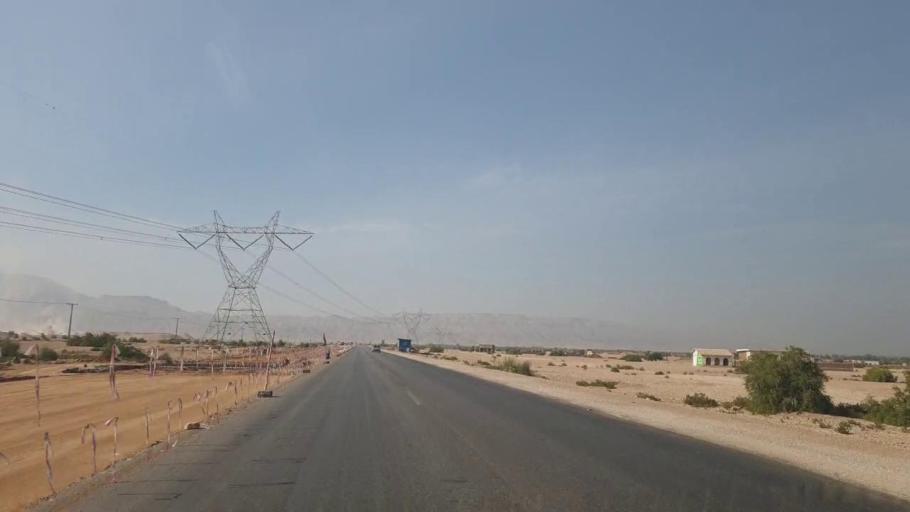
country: PK
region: Sindh
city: Sehwan
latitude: 26.2084
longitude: 67.9267
